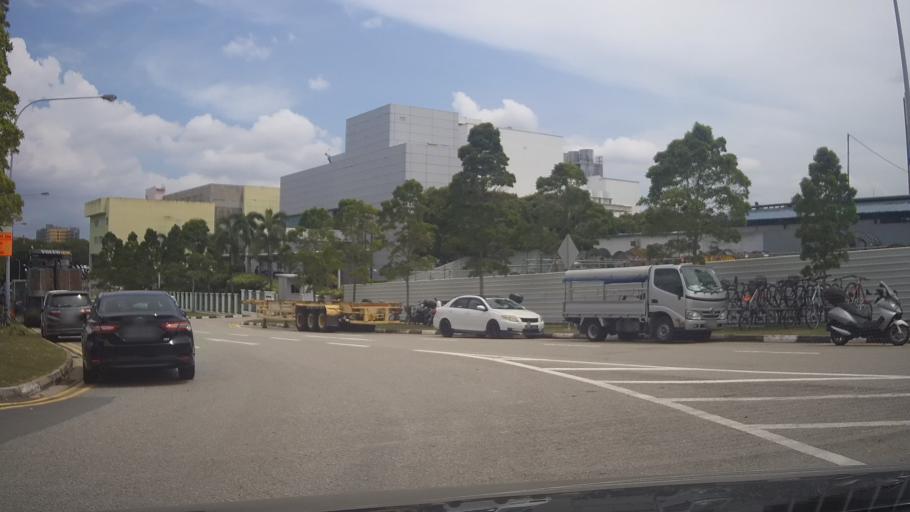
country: MY
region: Johor
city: Johor Bahru
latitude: 1.4565
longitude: 103.7931
